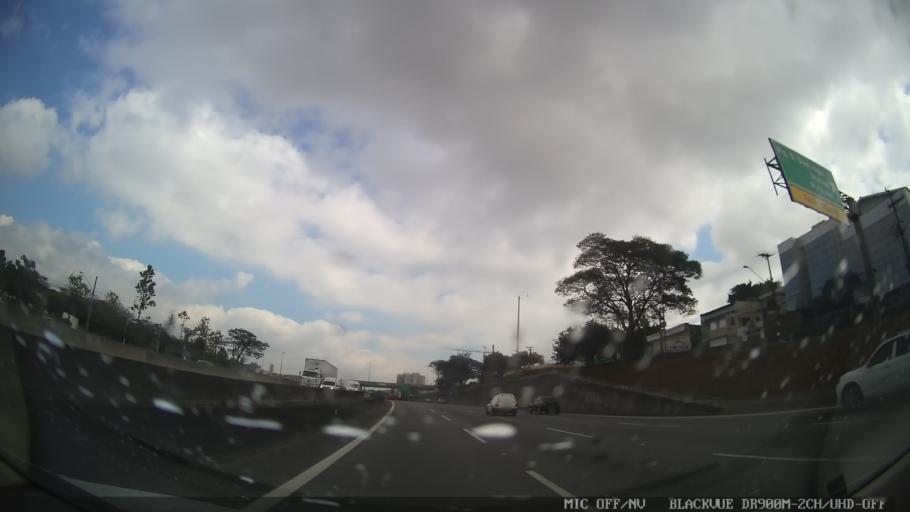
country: BR
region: Sao Paulo
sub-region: Osasco
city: Osasco
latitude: -23.5080
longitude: -46.7337
